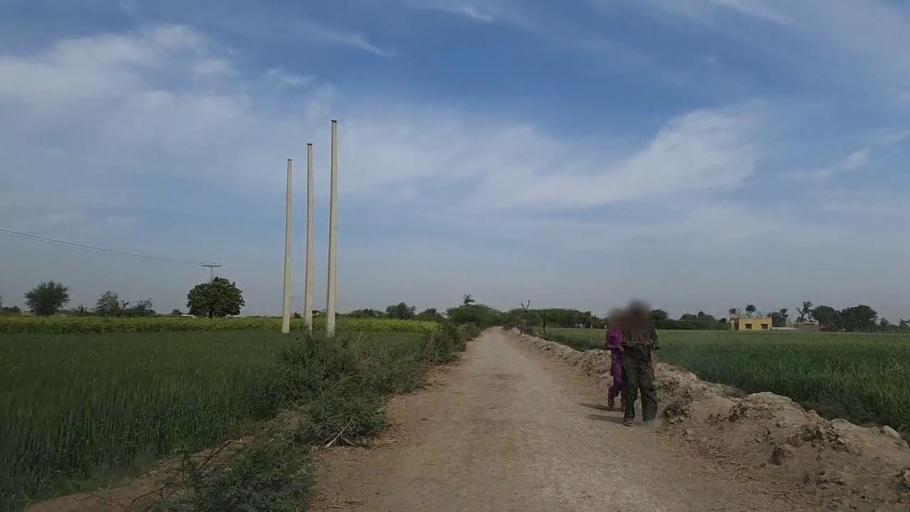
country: PK
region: Sindh
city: Samaro
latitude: 25.2979
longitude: 69.4239
